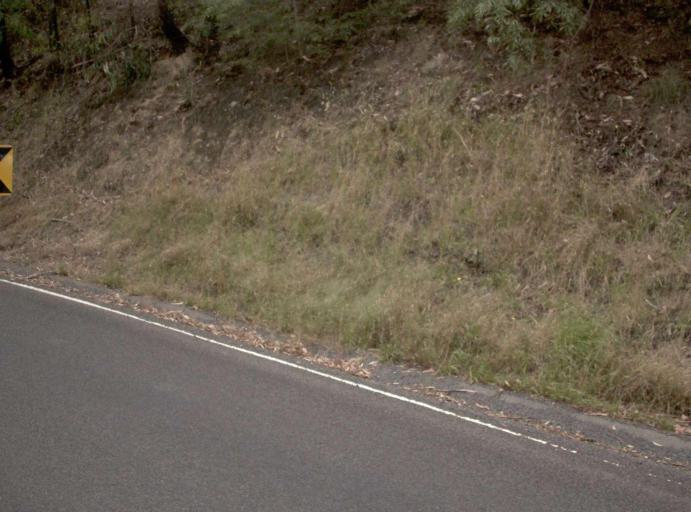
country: AU
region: Victoria
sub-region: Yarra Ranges
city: Healesville
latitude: -37.6416
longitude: 145.5776
